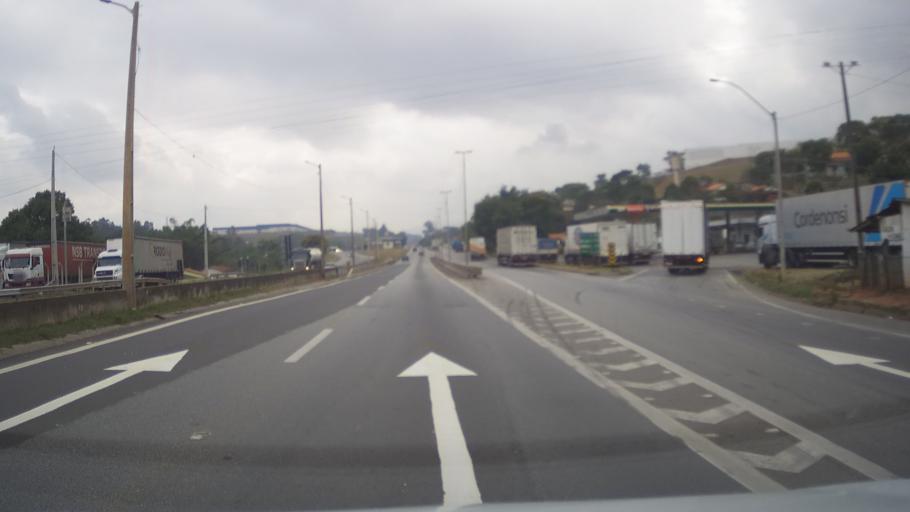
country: BR
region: Minas Gerais
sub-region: Extrema
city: Extrema
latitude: -22.8738
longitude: -46.3645
